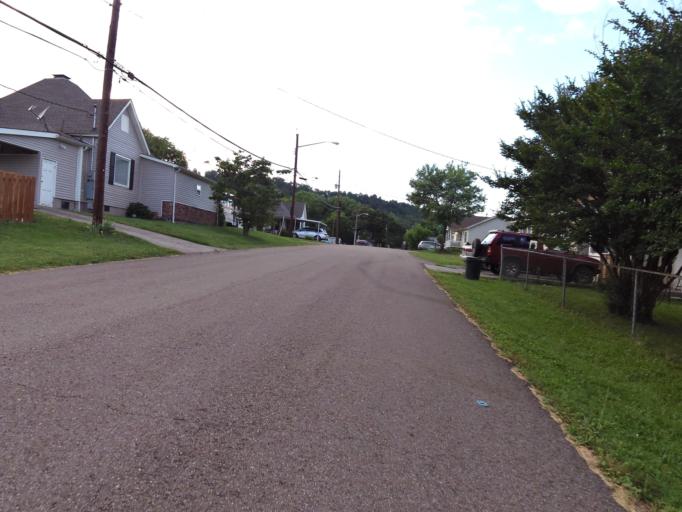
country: US
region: Tennessee
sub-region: Knox County
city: Knoxville
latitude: 35.9990
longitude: -83.9337
